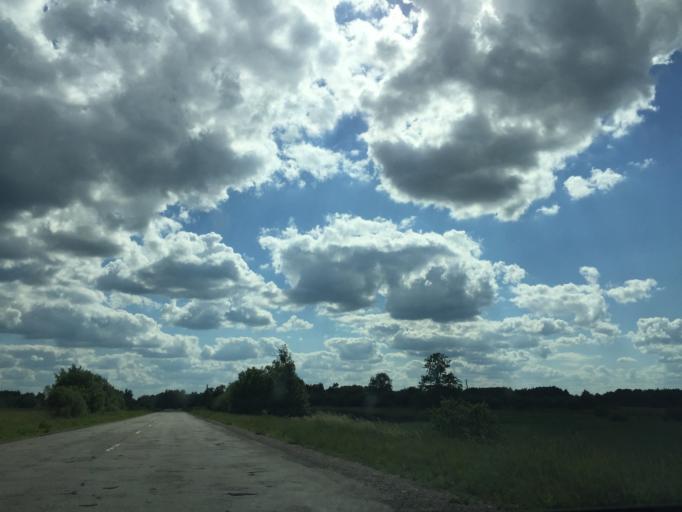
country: LV
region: Tukuma Rajons
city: Tukums
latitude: 56.8702
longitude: 23.0656
